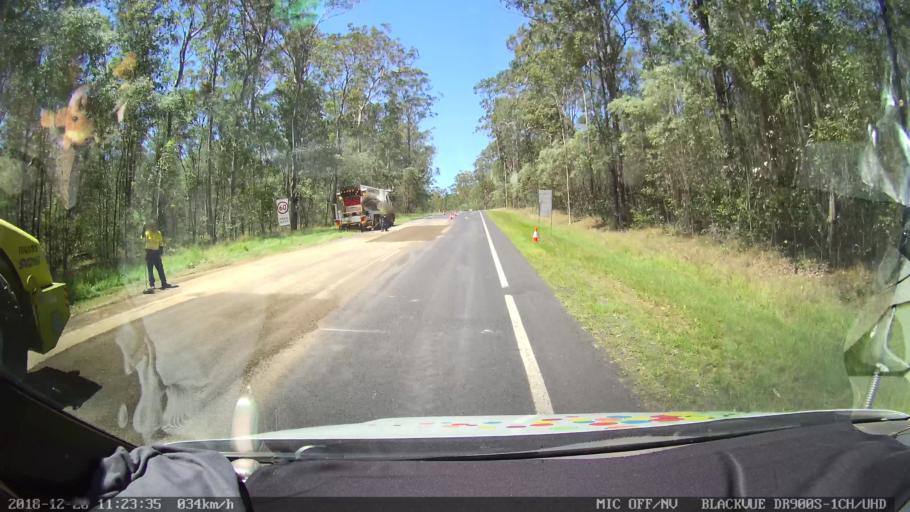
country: AU
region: New South Wales
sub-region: Richmond Valley
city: Casino
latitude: -29.0663
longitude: 153.0041
